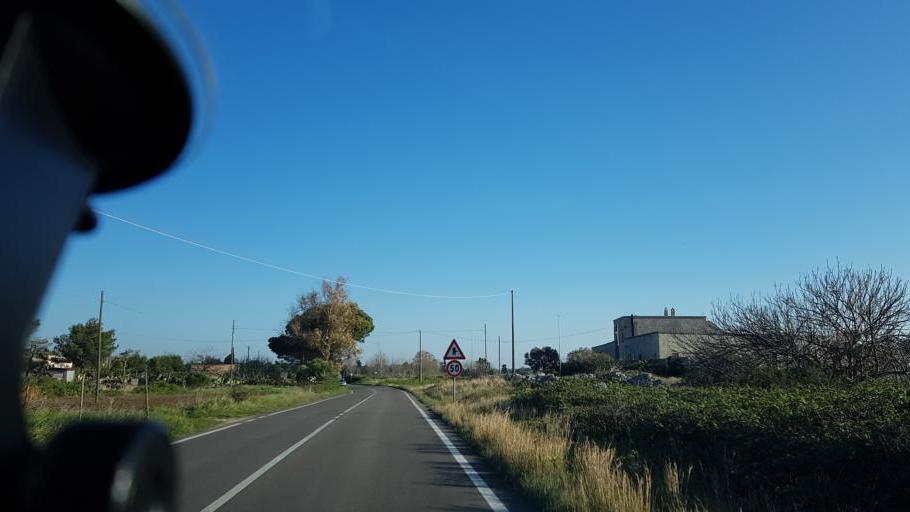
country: IT
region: Apulia
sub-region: Provincia di Lecce
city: Merine
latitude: 40.4132
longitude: 18.2540
